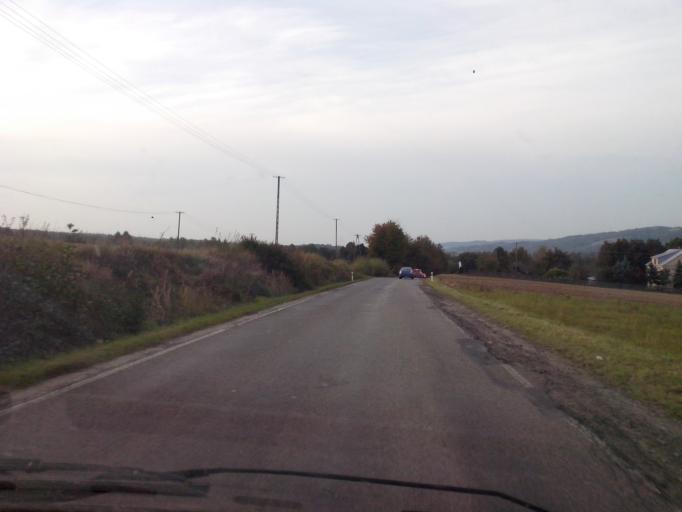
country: PL
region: Subcarpathian Voivodeship
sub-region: Powiat strzyzowski
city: Jawornik
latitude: 49.8194
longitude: 21.8347
